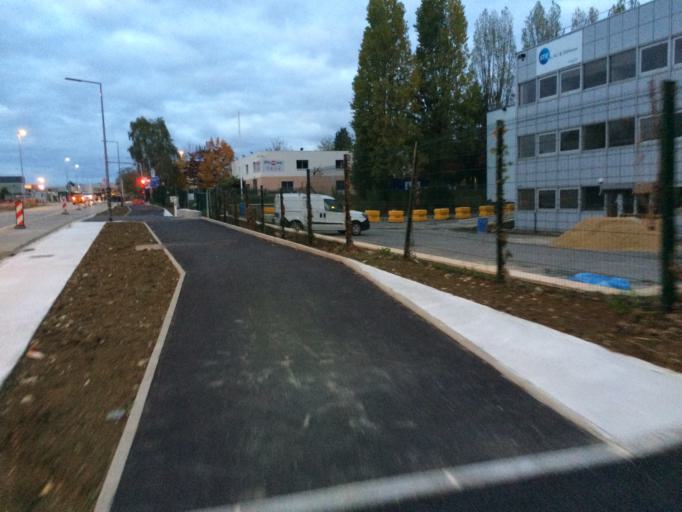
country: FR
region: Ile-de-France
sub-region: Departement de l'Essonne
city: Orsay
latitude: 48.6872
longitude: 2.2061
